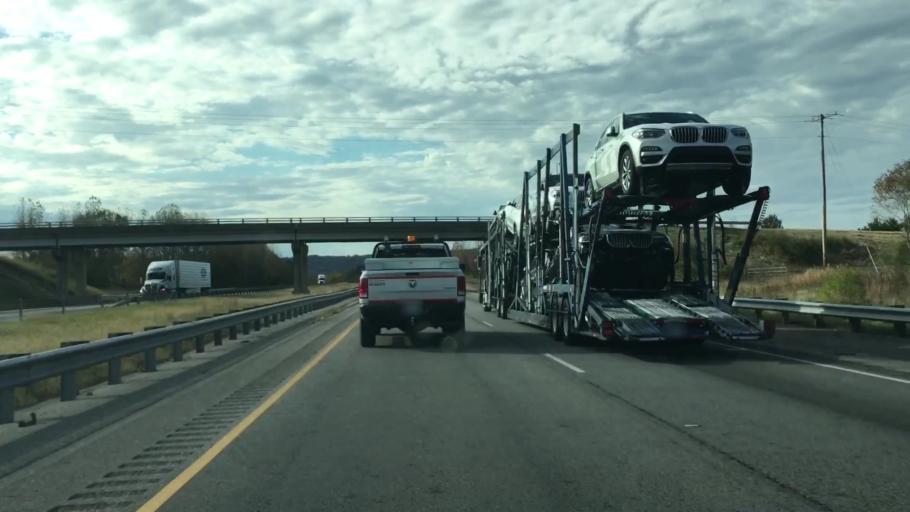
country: US
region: Arkansas
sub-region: Pope County
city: Atkins
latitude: 35.2508
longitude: -92.8888
